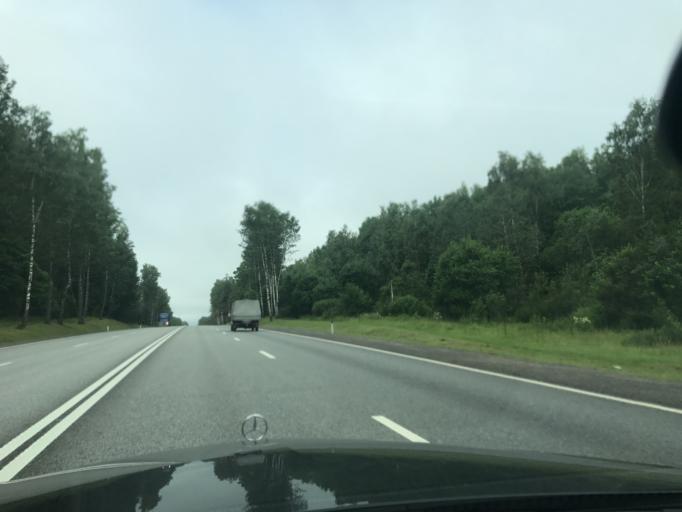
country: RU
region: Smolensk
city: Vyaz'ma
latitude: 55.3130
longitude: 34.5248
